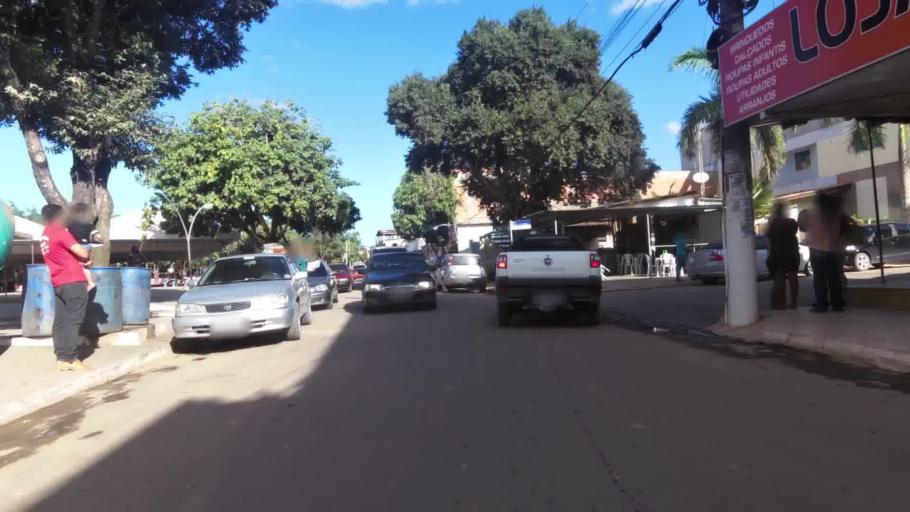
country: BR
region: Espirito Santo
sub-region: Marataizes
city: Marataizes
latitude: -21.0998
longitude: -41.0454
